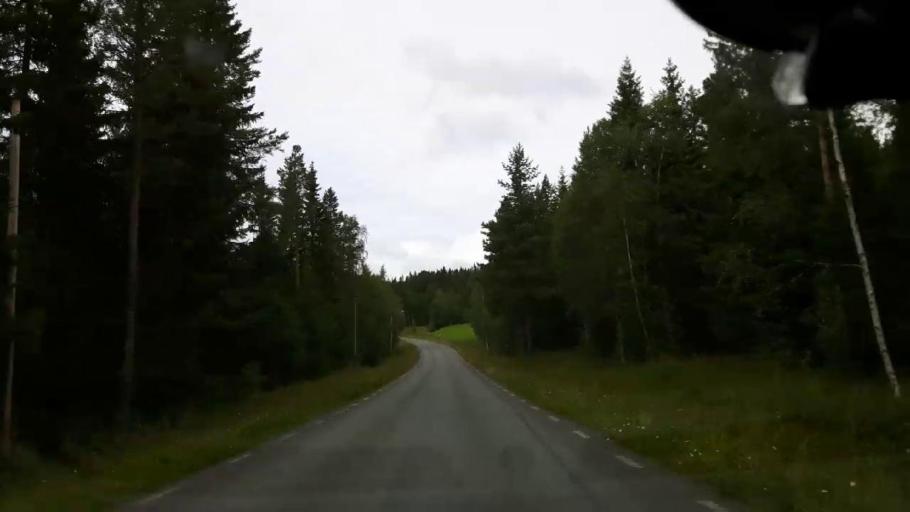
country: SE
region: Jaemtland
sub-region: Krokoms Kommun
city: Valla
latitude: 63.4797
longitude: 14.0604
